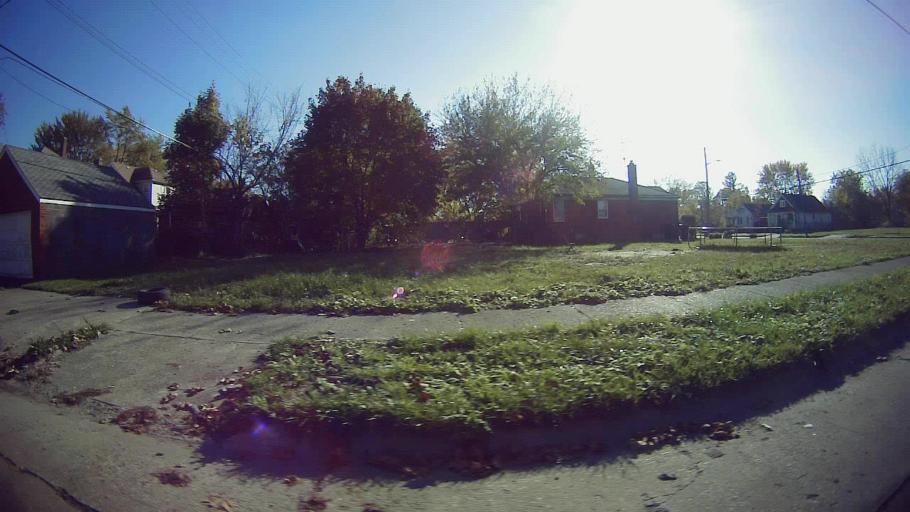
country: US
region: Michigan
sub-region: Macomb County
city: Eastpointe
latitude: 42.4370
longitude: -82.9831
